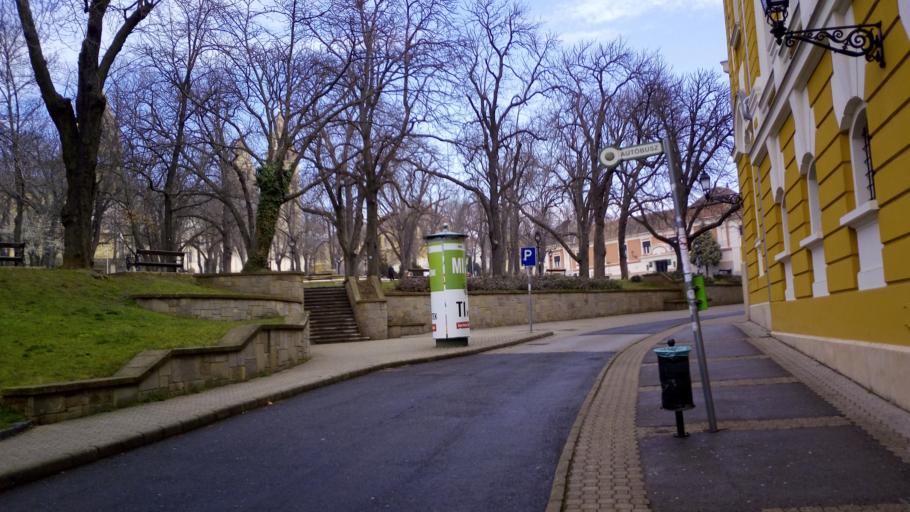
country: HU
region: Baranya
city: Pecs
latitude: 46.0765
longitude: 18.2229
